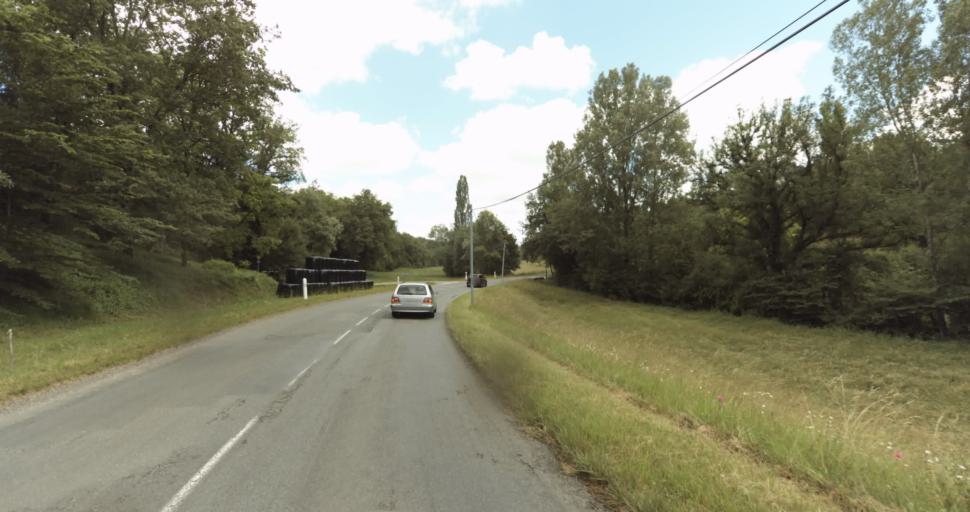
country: FR
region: Aquitaine
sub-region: Departement de la Dordogne
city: Beaumont-du-Perigord
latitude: 44.7534
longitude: 0.7605
